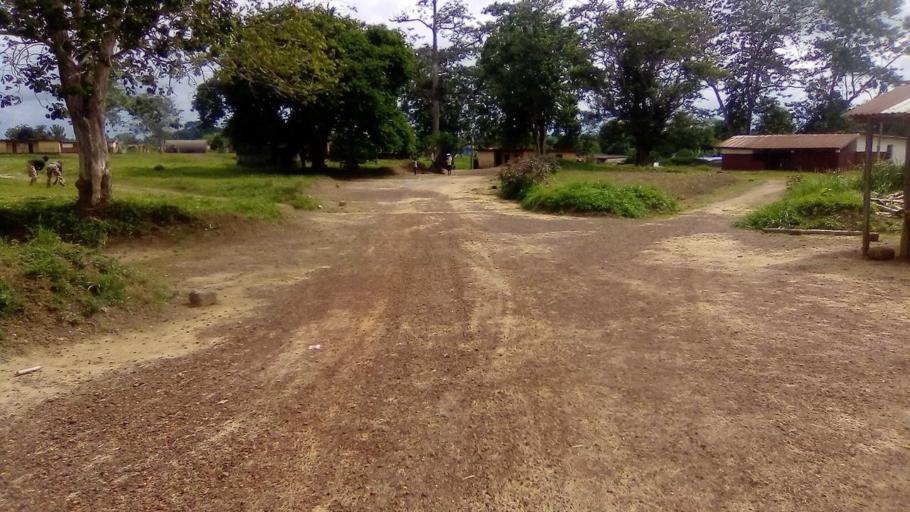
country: SL
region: Southern Province
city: Pujehun
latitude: 7.3685
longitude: -11.7258
